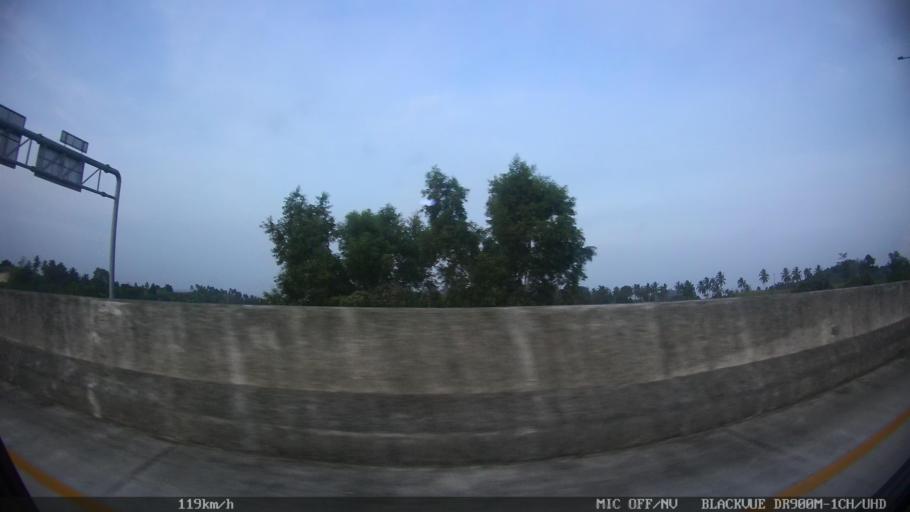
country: ID
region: Lampung
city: Penengahan
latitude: -5.8007
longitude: 105.7299
